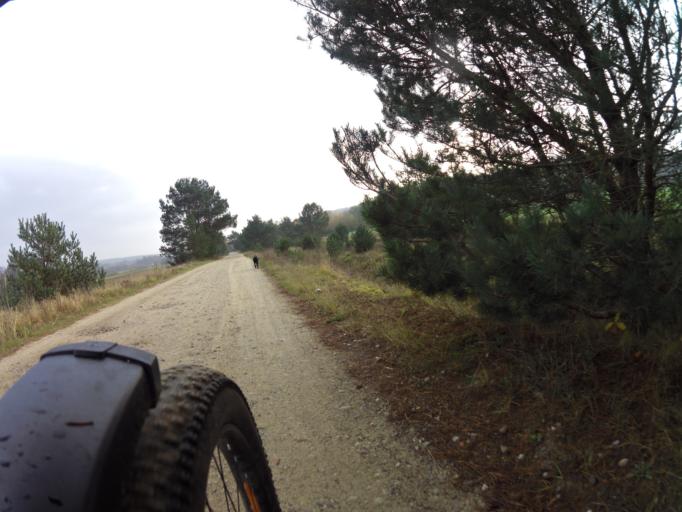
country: PL
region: Pomeranian Voivodeship
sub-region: Powiat wejherowski
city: Gniewino
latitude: 54.7059
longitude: 18.1031
